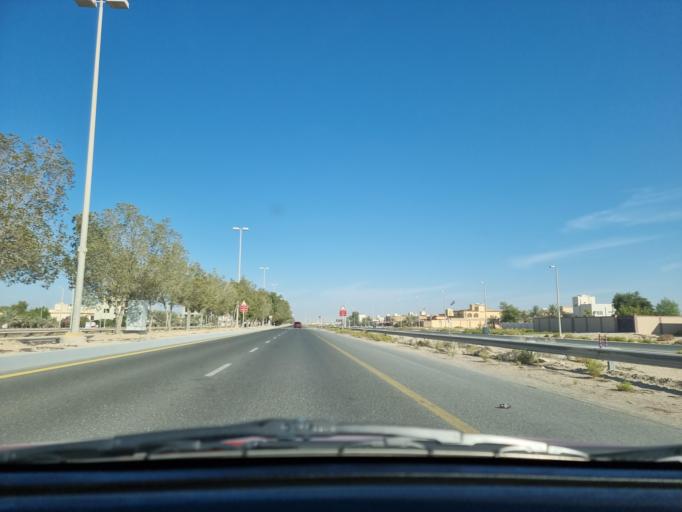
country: AE
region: Abu Dhabi
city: Abu Dhabi
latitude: 24.3905
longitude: 54.6948
